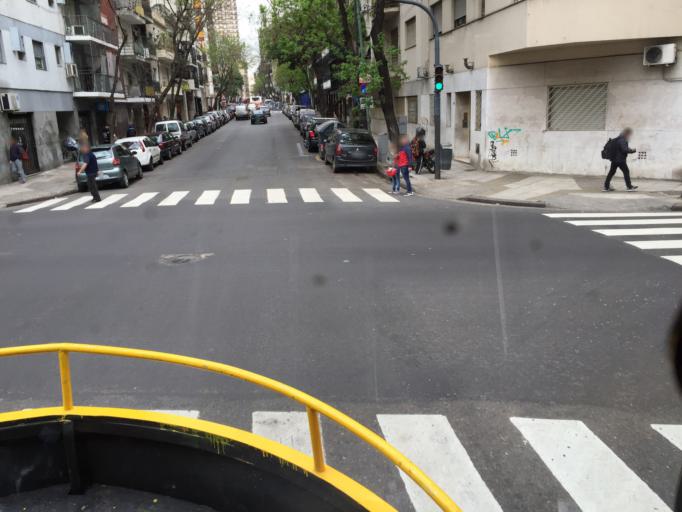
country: AR
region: Buenos Aires F.D.
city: Buenos Aires
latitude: -34.6052
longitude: -58.4095
